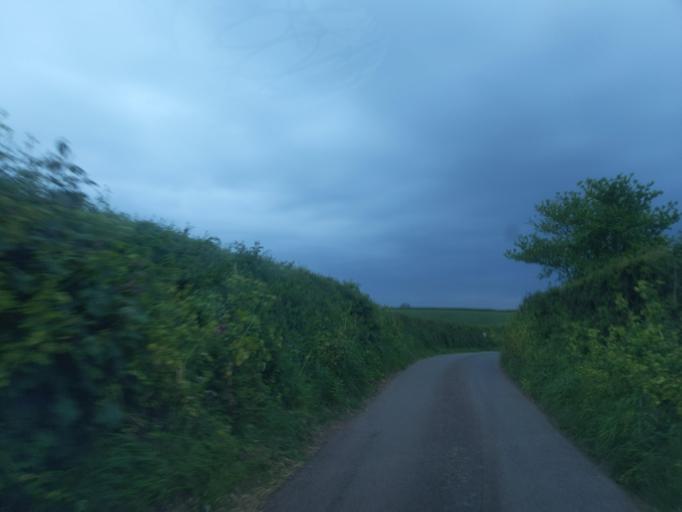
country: GB
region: England
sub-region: Borough of Torbay
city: Brixham
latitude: 50.3581
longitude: -3.5366
